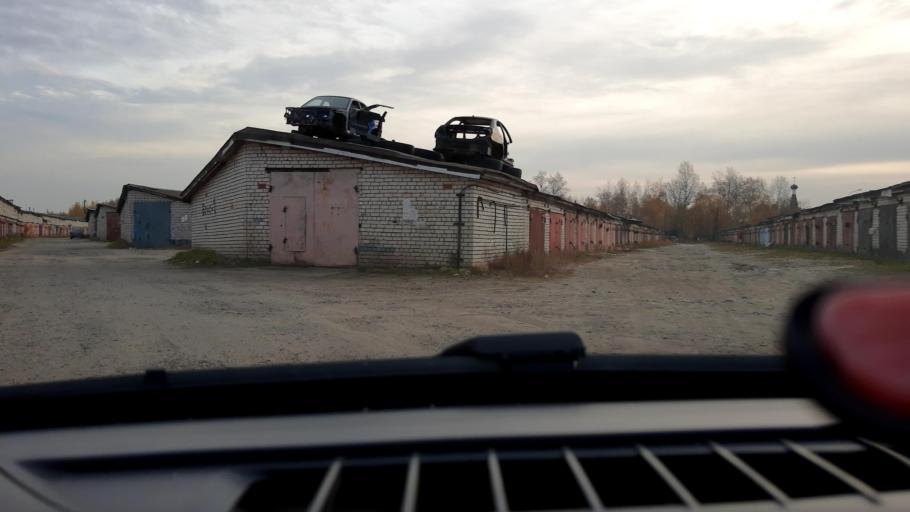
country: RU
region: Nizjnij Novgorod
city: Gorbatovka
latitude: 56.3312
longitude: 43.8153
